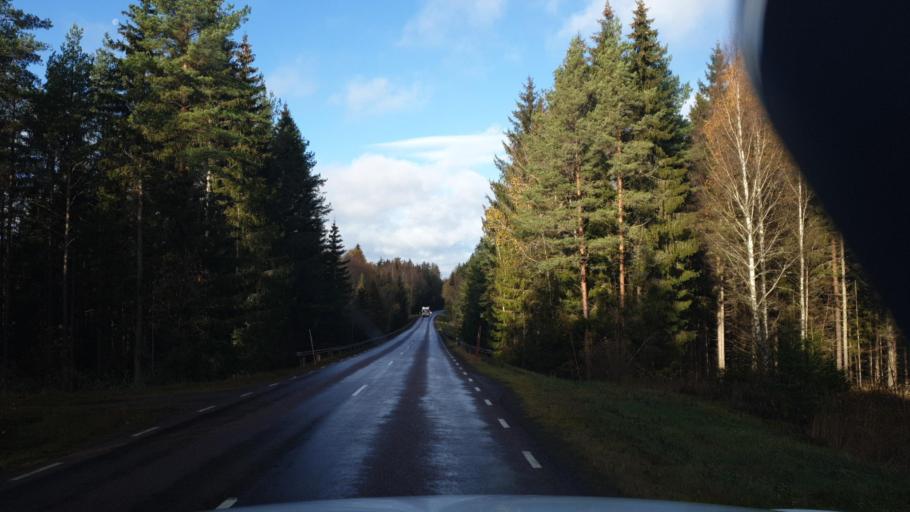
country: SE
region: Vaermland
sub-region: Grums Kommun
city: Grums
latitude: 59.4030
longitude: 13.0127
